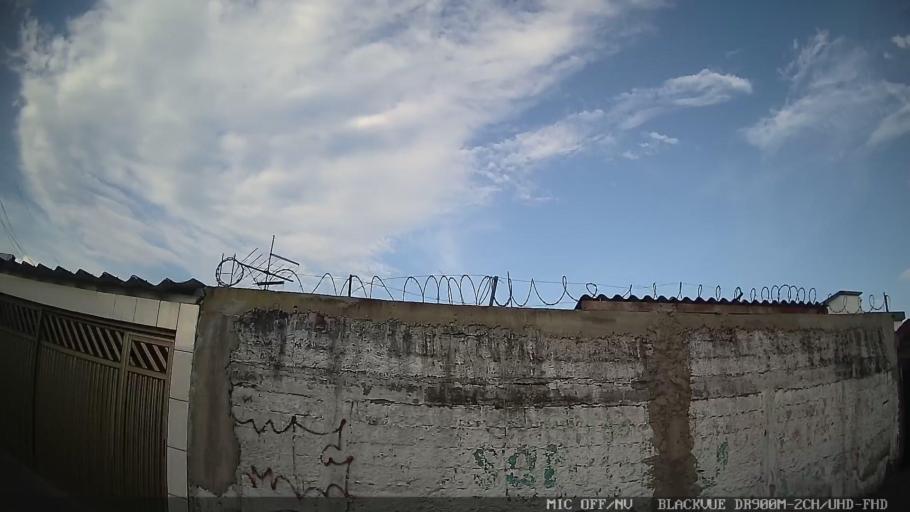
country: BR
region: Sao Paulo
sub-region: Cubatao
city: Cubatao
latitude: -23.8918
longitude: -46.4210
